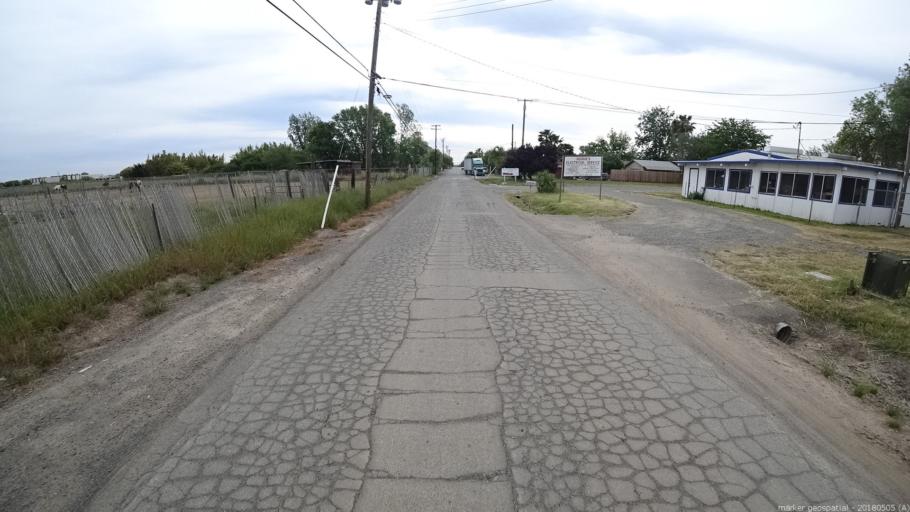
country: US
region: California
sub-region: Sacramento County
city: Rio Linda
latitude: 38.6583
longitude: -121.4341
